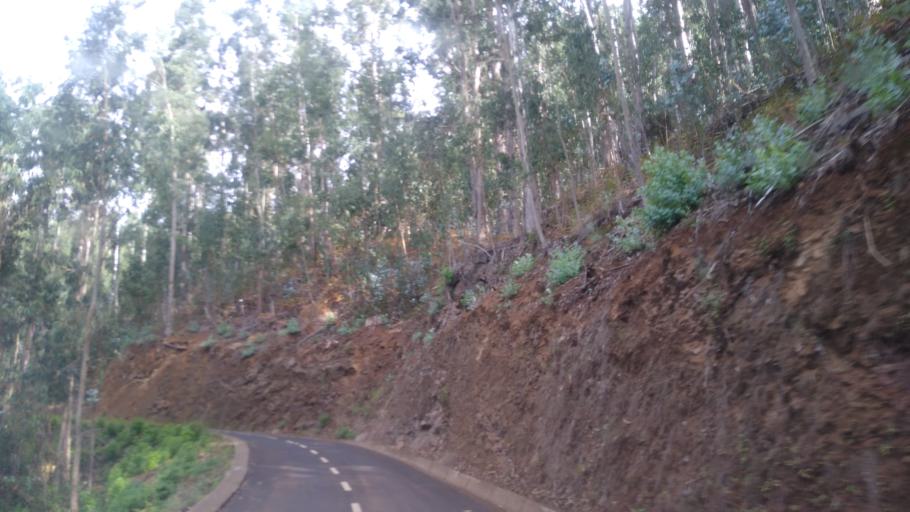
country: PT
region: Madeira
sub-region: Camara de Lobos
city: Curral das Freiras
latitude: 32.6952
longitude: -16.9410
